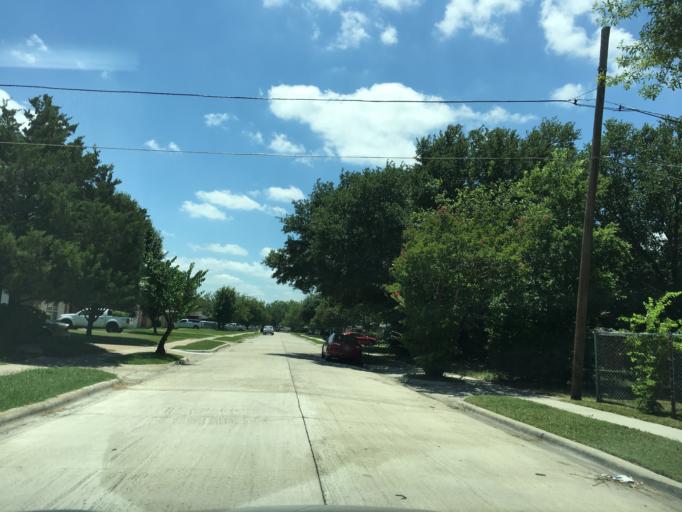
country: US
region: Texas
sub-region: Dallas County
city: Garland
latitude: 32.8333
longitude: -96.6481
